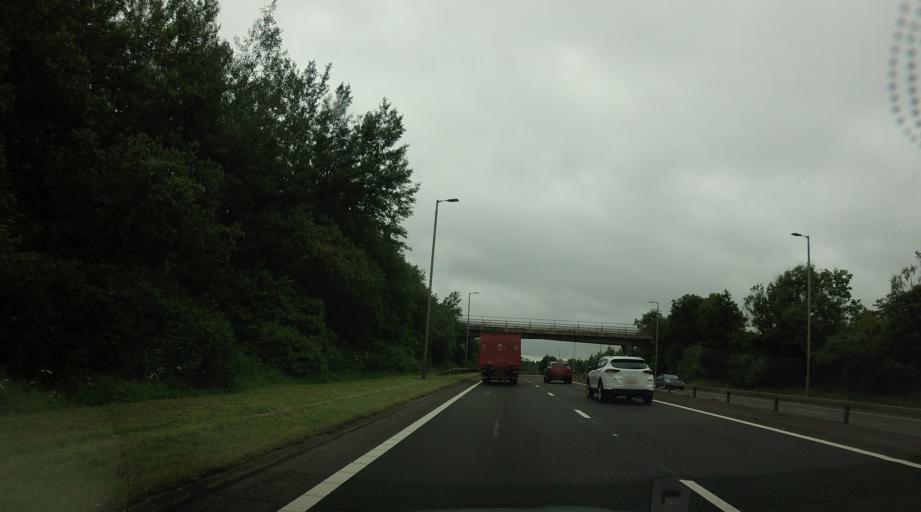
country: GB
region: Scotland
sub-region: South Lanarkshire
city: High Blantyre
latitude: 55.7827
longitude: -4.1172
